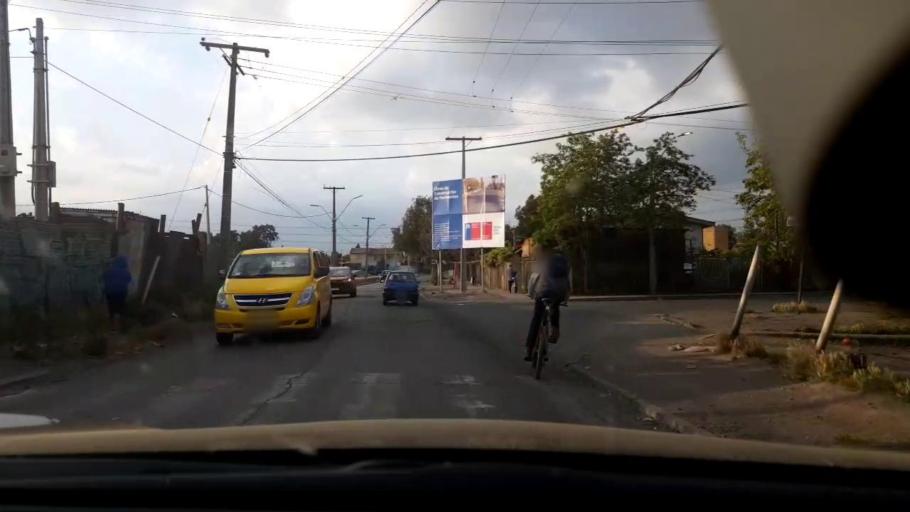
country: CL
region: Santiago Metropolitan
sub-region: Provincia de Santiago
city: Lo Prado
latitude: -33.4269
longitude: -70.7509
